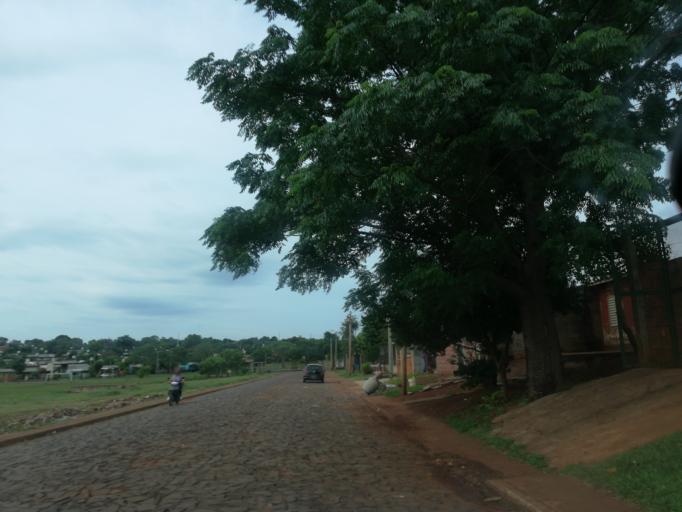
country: AR
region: Misiones
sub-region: Departamento de Capital
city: Posadas
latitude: -27.4303
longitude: -55.9093
